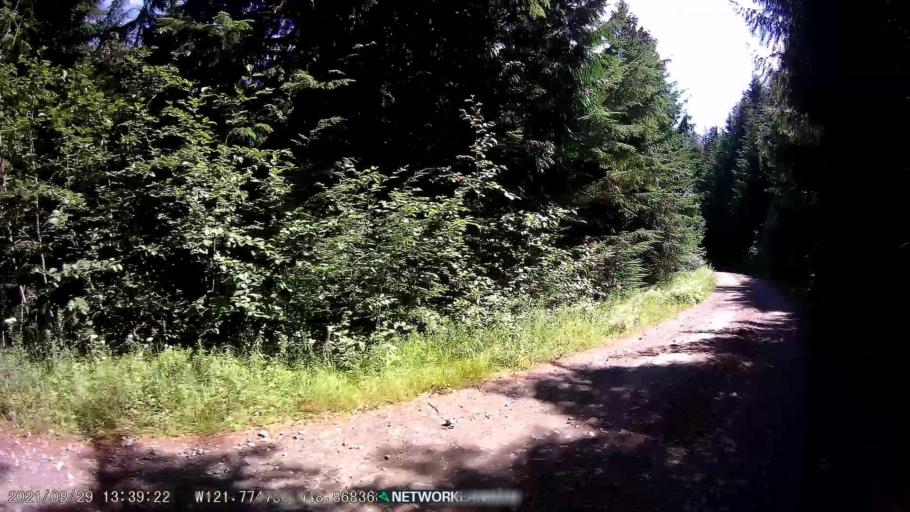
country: CA
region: British Columbia
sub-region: Fraser Valley Regional District
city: Chilliwack
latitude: 48.8683
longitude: -121.7747
